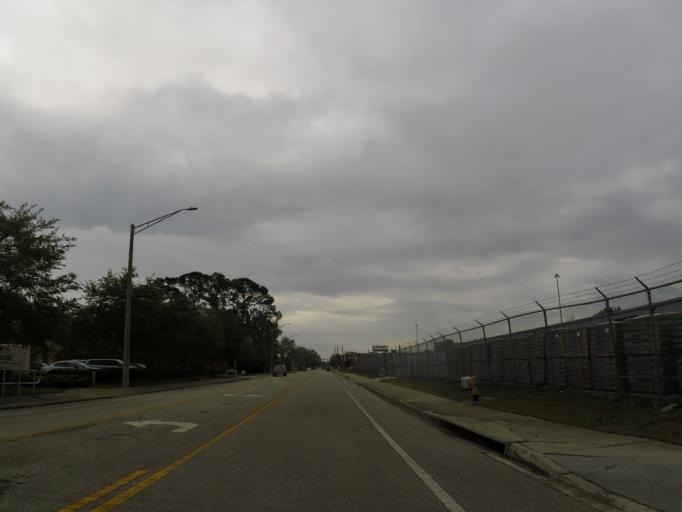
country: US
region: Florida
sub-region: Duval County
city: Jacksonville
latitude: 30.2725
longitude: -81.6127
